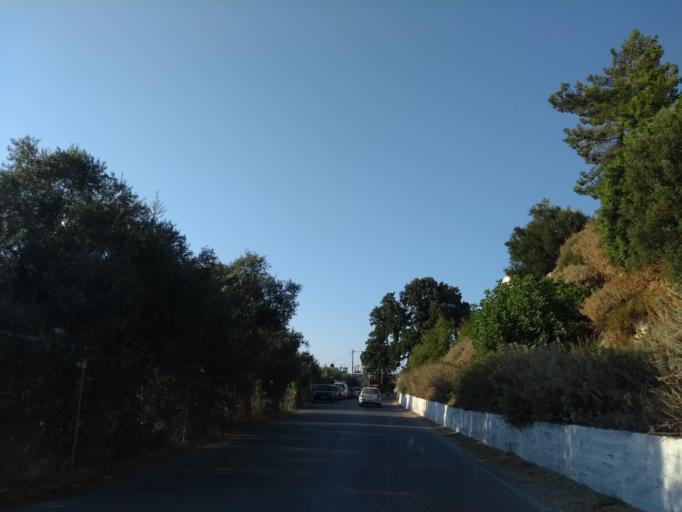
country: GR
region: Crete
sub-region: Nomos Chanias
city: Kalivai
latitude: 35.4350
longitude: 24.1770
